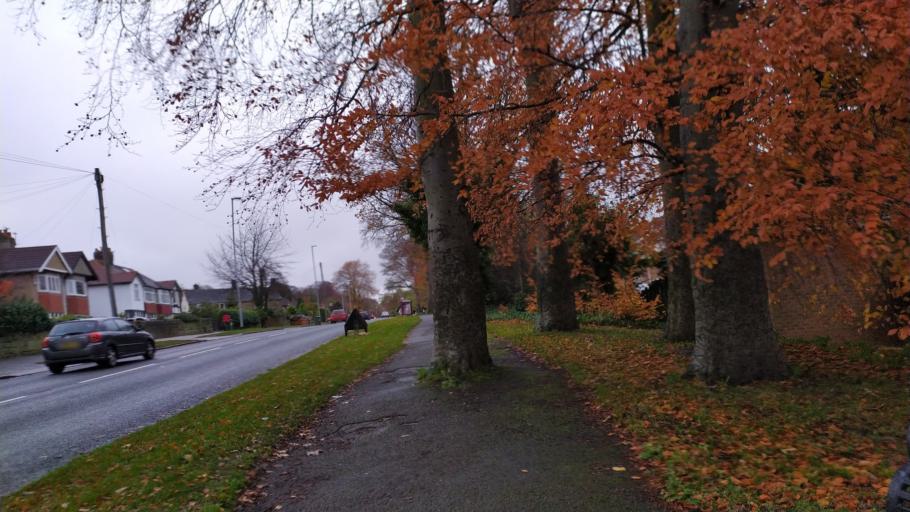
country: GB
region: England
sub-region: City and Borough of Leeds
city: Chapel Allerton
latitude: 53.8305
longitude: -1.5636
